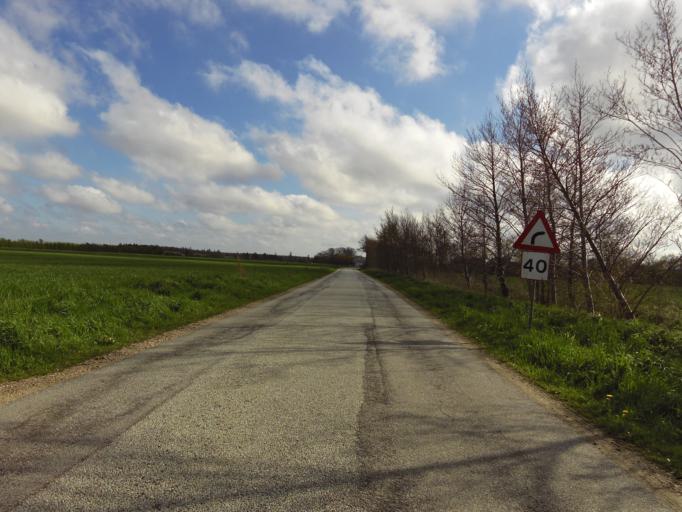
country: DK
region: South Denmark
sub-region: Haderslev Kommune
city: Gram
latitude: 55.3106
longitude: 8.9780
